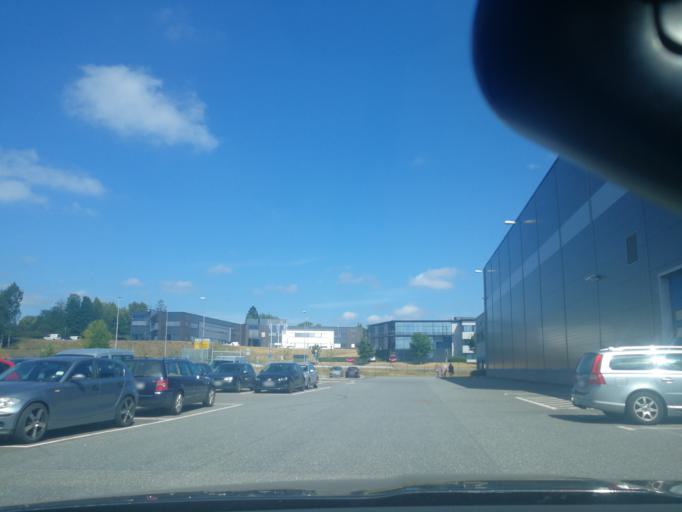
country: NO
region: Vestfold
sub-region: Sandefjord
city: Sandefjord
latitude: 59.1759
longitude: 10.2185
